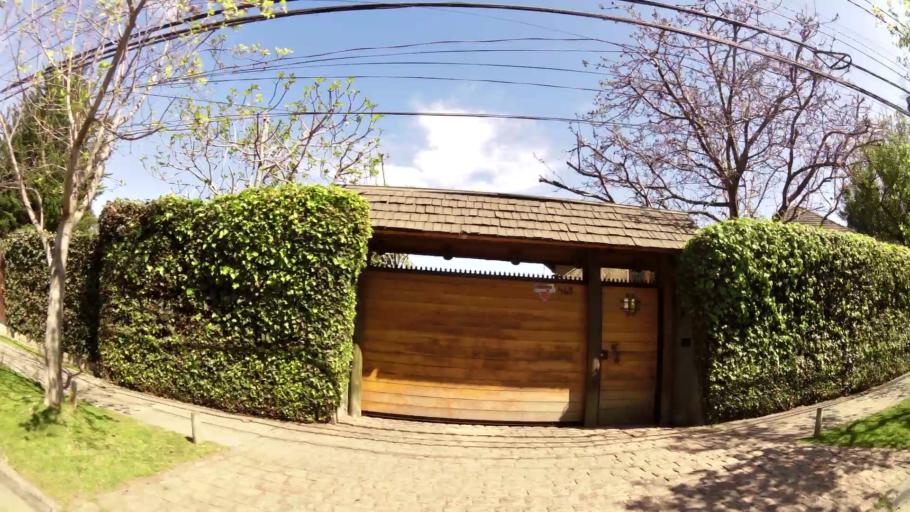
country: CL
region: Santiago Metropolitan
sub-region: Provincia de Santiago
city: Villa Presidente Frei, Nunoa, Santiago, Chile
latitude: -33.4498
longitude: -70.5239
